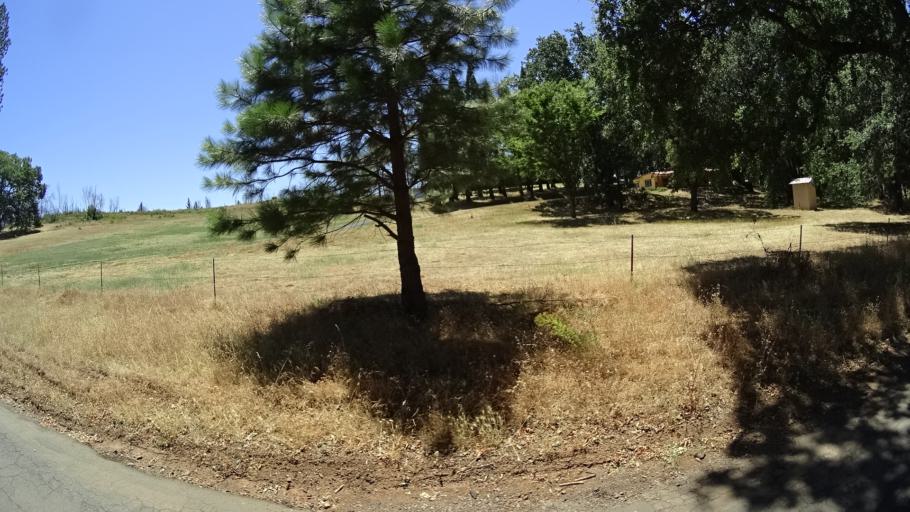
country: US
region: California
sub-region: Calaveras County
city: Mountain Ranch
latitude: 38.2416
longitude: -120.5684
